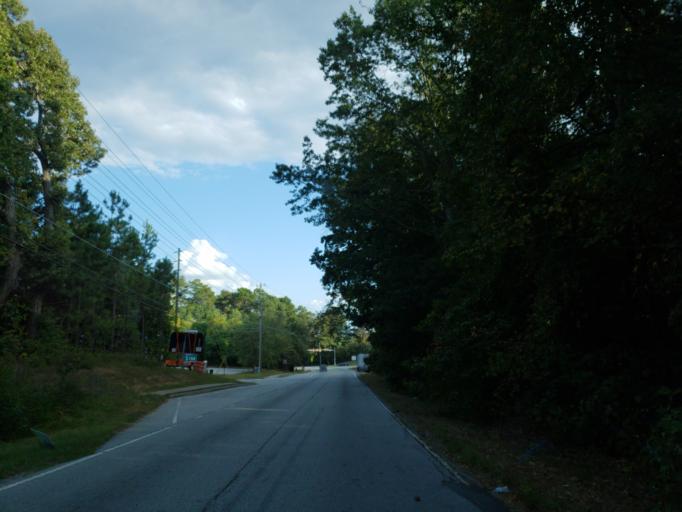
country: US
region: Georgia
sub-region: Cobb County
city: Mableton
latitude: 33.7528
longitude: -84.5822
